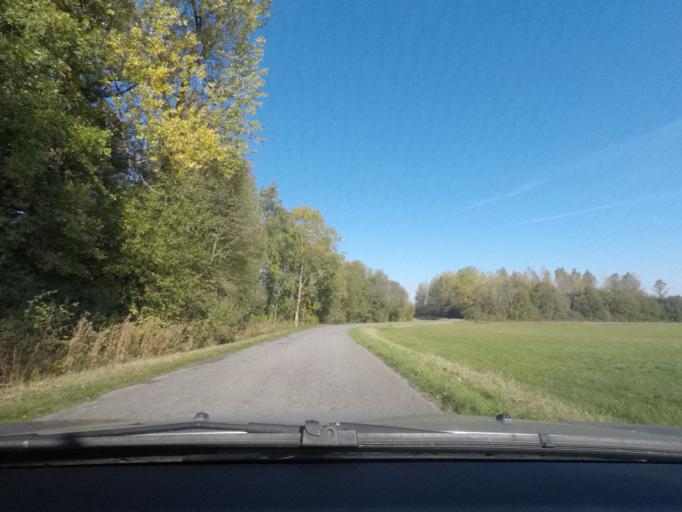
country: BE
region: Wallonia
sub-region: Province du Luxembourg
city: Etalle
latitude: 49.7060
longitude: 5.5676
